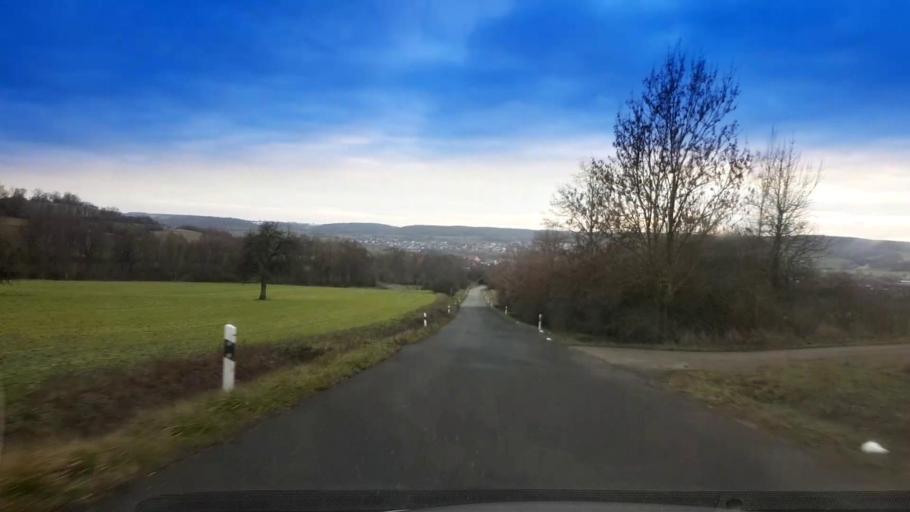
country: DE
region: Bavaria
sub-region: Upper Franconia
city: Lauter
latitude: 49.9539
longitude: 10.7591
